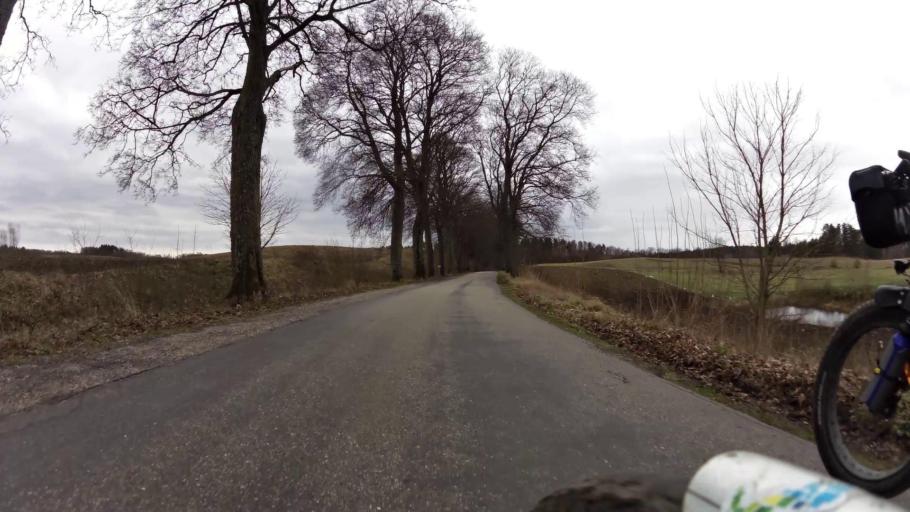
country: PL
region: Pomeranian Voivodeship
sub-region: Powiat bytowski
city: Trzebielino
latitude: 54.1013
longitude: 17.1313
